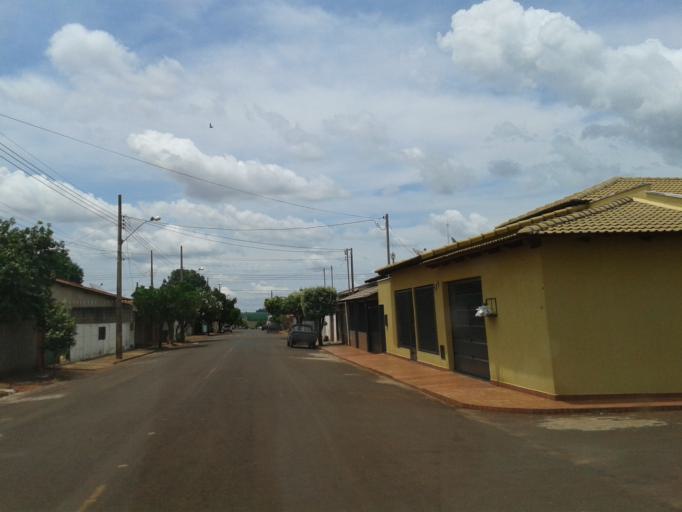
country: BR
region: Minas Gerais
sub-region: Centralina
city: Centralina
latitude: -18.7230
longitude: -49.1991
